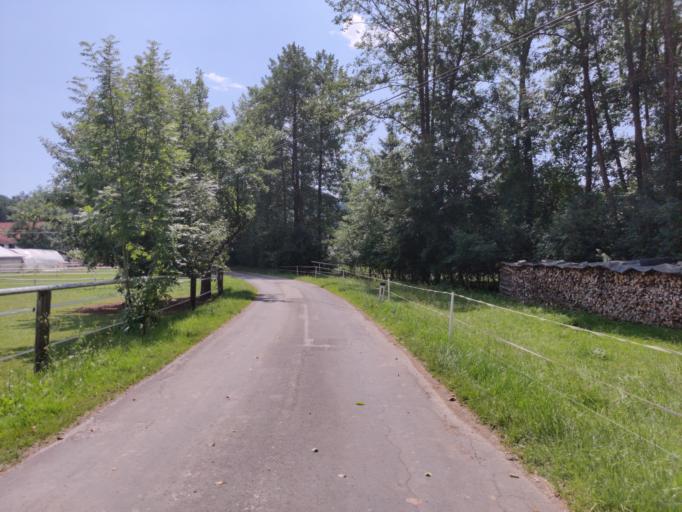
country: AT
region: Styria
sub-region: Politischer Bezirk Graz-Umgebung
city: Eisbach
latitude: 47.1050
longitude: 15.2889
